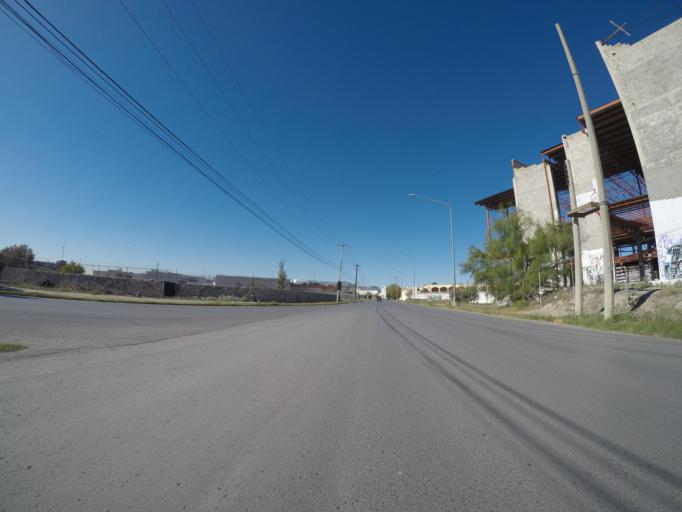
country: MX
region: Chihuahua
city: Ciudad Juarez
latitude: 31.7431
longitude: -106.4500
